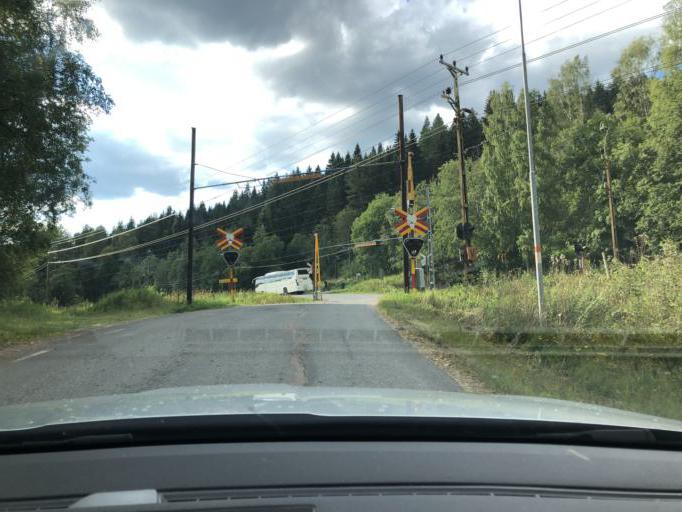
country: SE
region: Vaesternorrland
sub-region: Solleftea Kommun
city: Solleftea
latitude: 63.2115
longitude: 17.1871
